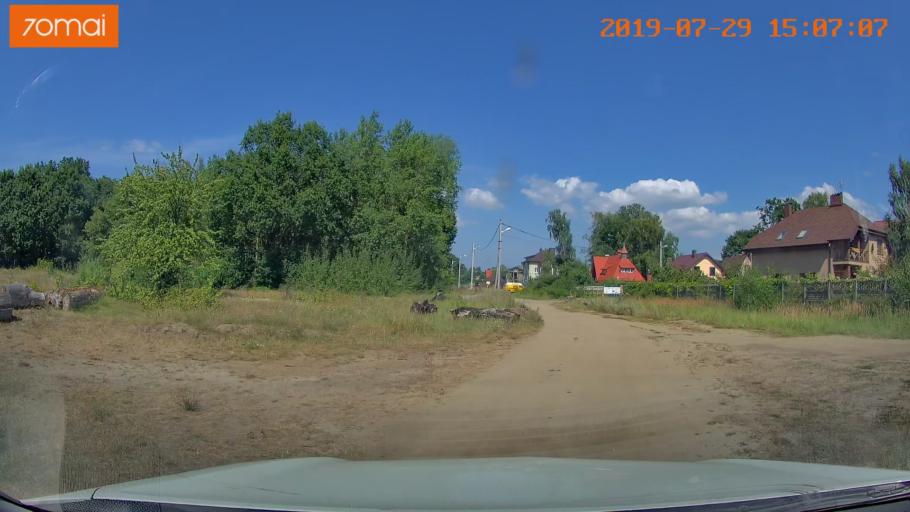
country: RU
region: Kaliningrad
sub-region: Gorod Kaliningrad
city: Baltiysk
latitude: 54.6765
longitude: 19.9135
